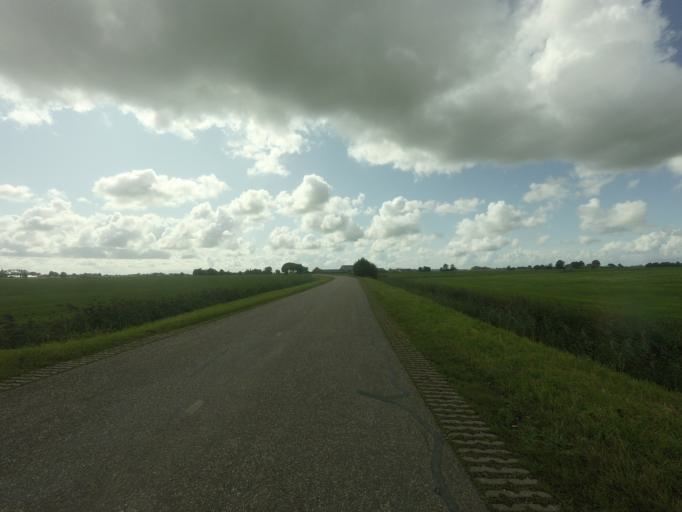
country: NL
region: Friesland
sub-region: Sudwest Fryslan
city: IJlst
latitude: 53.0564
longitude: 5.6176
